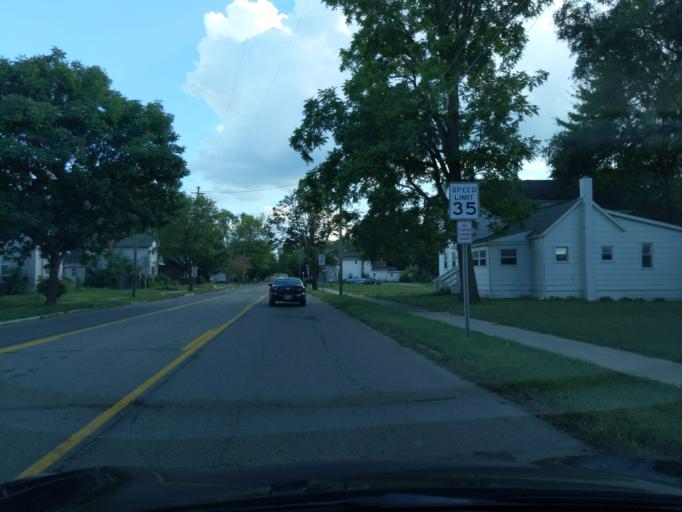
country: US
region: Michigan
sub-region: Jackson County
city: Jackson
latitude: 42.2535
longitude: -84.4025
